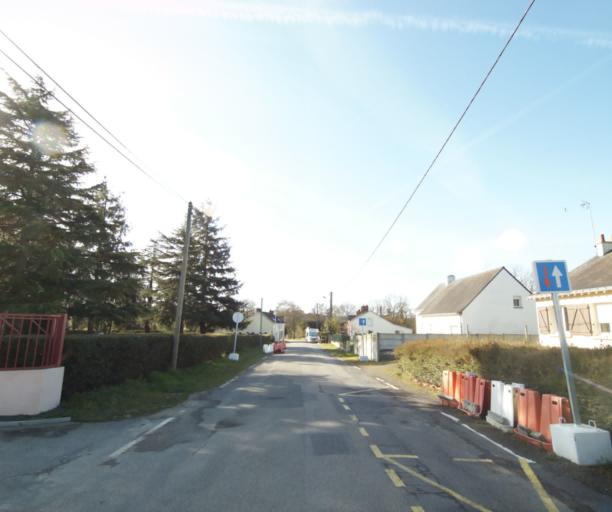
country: FR
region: Pays de la Loire
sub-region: Departement de la Loire-Atlantique
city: Bouvron
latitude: 47.4141
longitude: -1.8458
